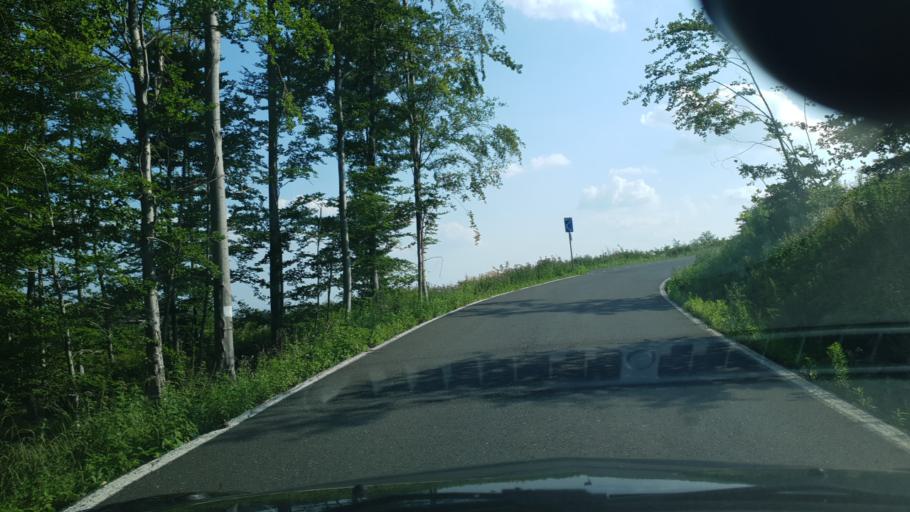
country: HR
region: Grad Zagreb
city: Kasina
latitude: 45.8858
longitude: 15.9696
